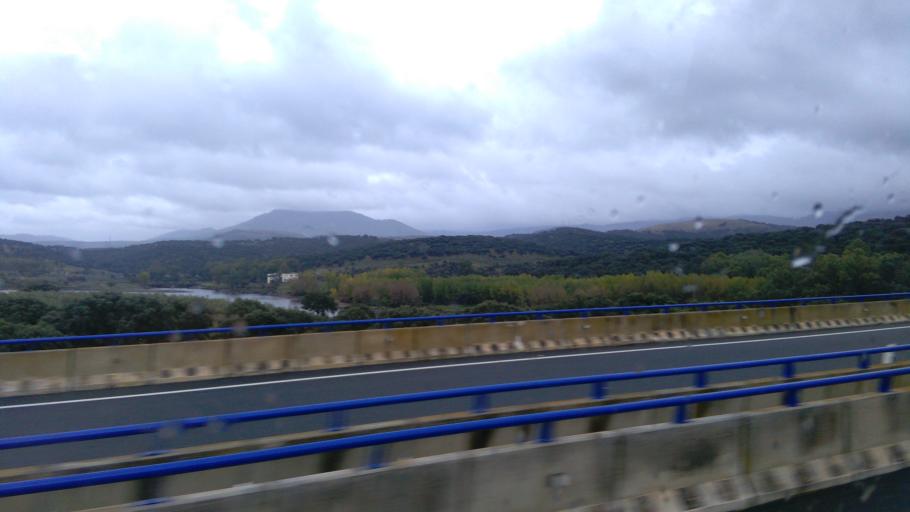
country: ES
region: Extremadura
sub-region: Provincia de Caceres
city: Romangordo
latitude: 39.7816
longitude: -5.7307
